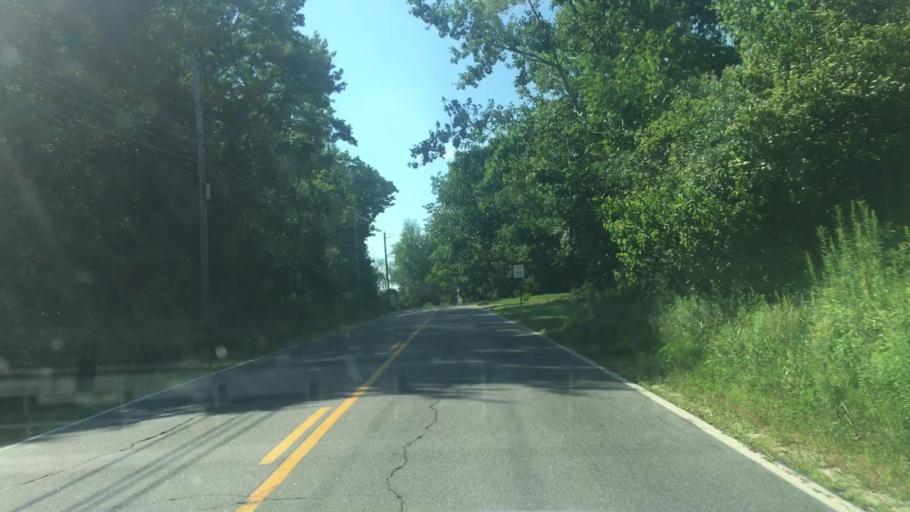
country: US
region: Maine
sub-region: York County
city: Hollis Center
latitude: 43.6398
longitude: -70.5817
